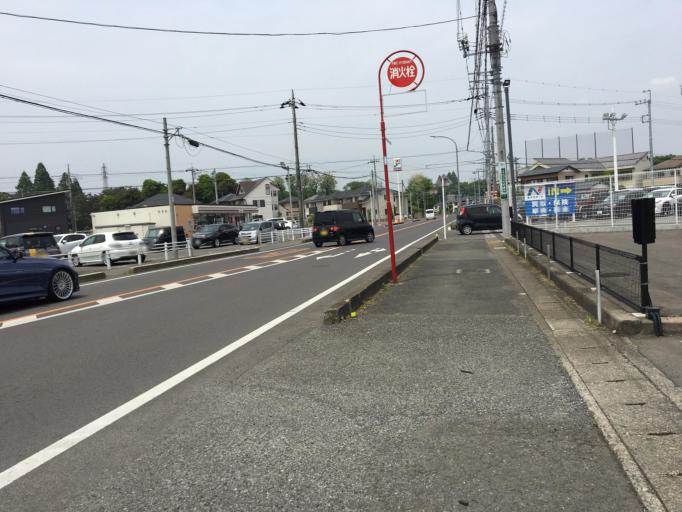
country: JP
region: Tochigi
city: Oyama
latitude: 36.3388
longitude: 139.8176
